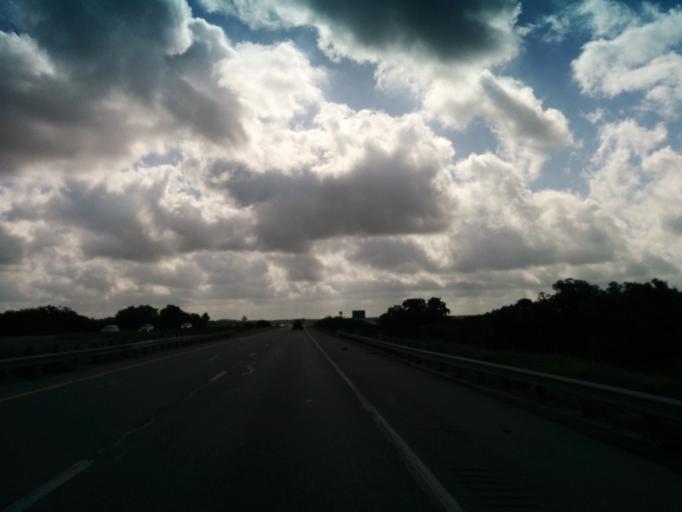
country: US
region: Texas
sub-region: Caldwell County
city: Luling
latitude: 29.6503
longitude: -97.6048
